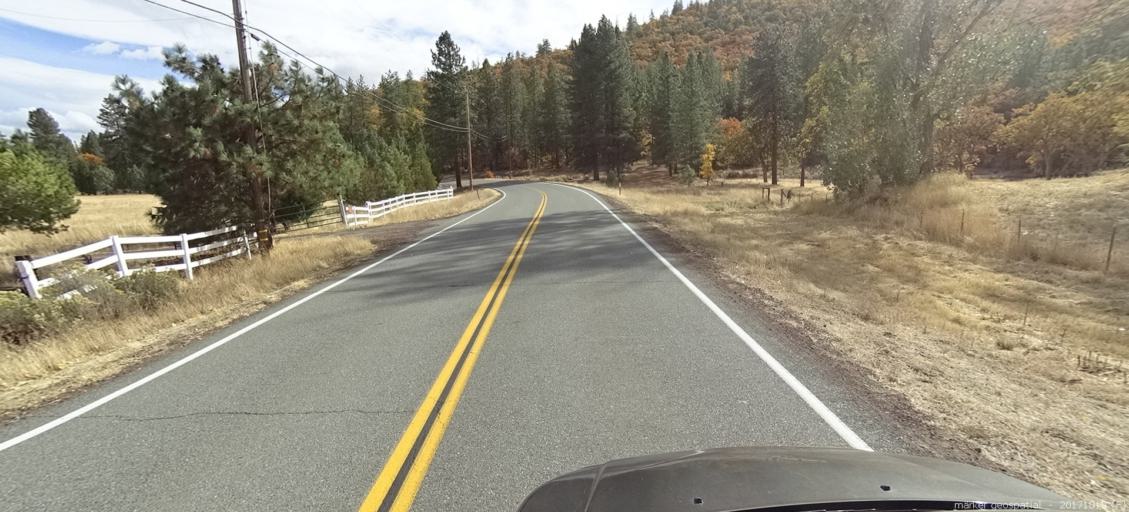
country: US
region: California
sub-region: Shasta County
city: Burney
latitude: 41.0361
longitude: -121.4940
